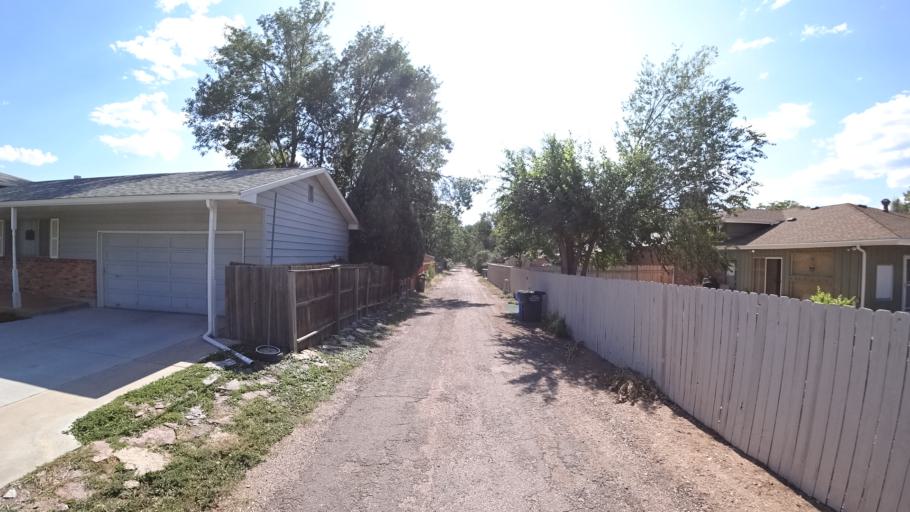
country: US
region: Colorado
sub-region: El Paso County
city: Colorado Springs
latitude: 38.8702
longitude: -104.8011
